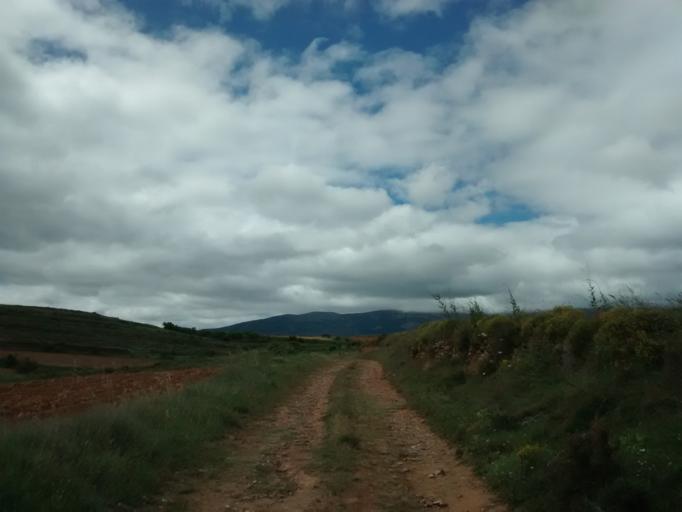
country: ES
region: Aragon
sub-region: Provincia de Zaragoza
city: Trasmoz
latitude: 41.8391
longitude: -1.7380
